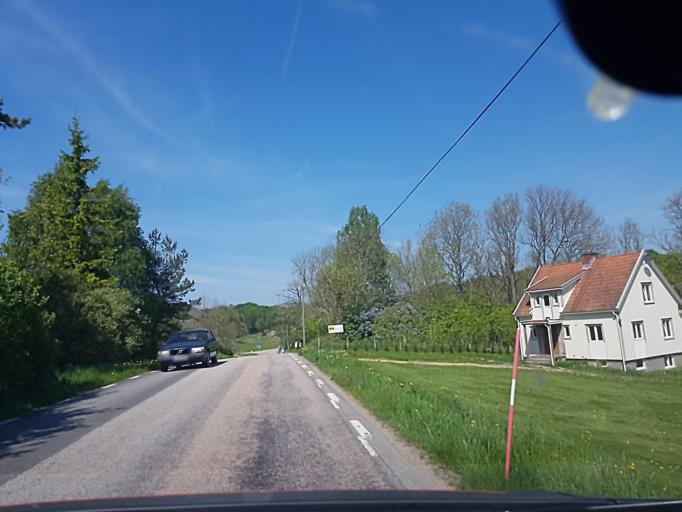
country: SE
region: Vaestra Goetaland
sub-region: Lysekils Kommun
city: Lysekil
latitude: 58.1564
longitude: 11.4612
